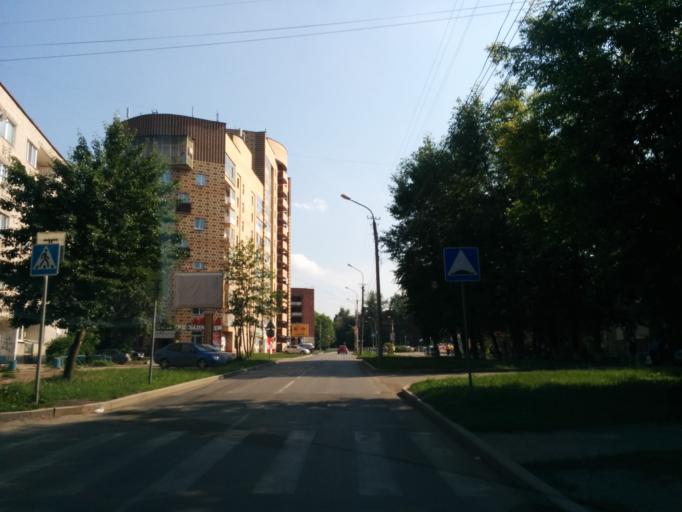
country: RU
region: Perm
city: Perm
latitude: 57.9983
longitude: 56.2086
